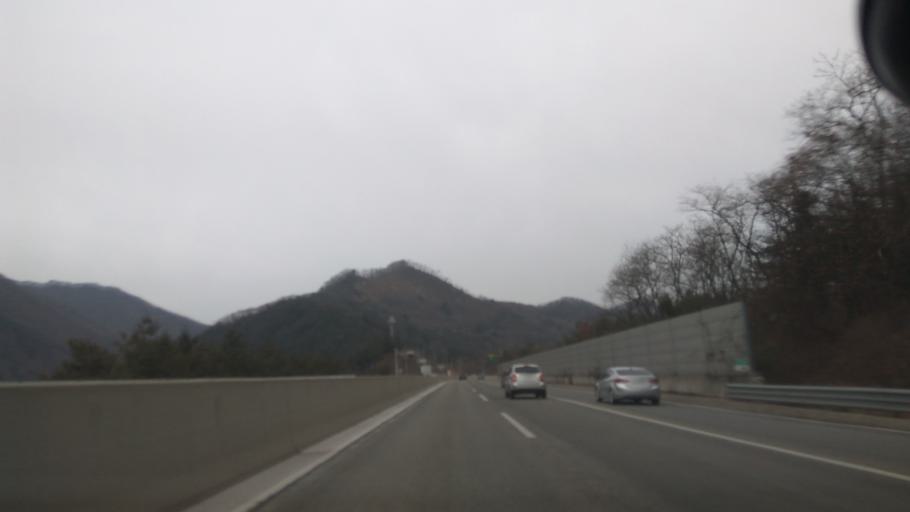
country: KR
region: Gyeonggi-do
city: Cheongpyeong
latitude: 37.6474
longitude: 127.4237
